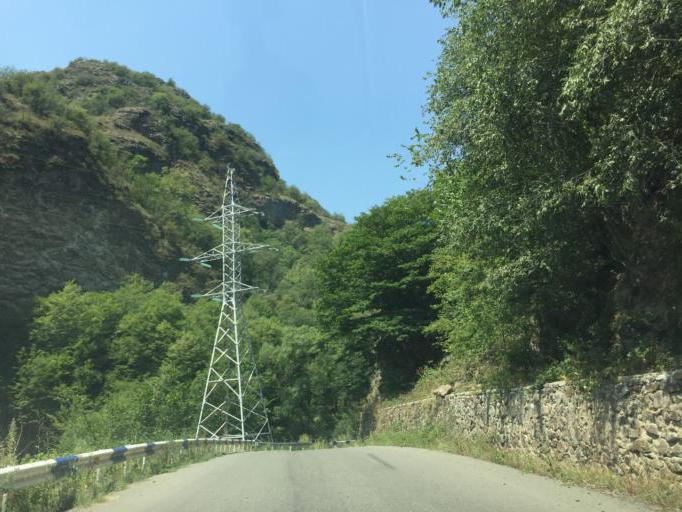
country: AZ
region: Kalbacar Rayonu
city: Kerbakhiar
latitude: 40.1273
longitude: 46.4013
